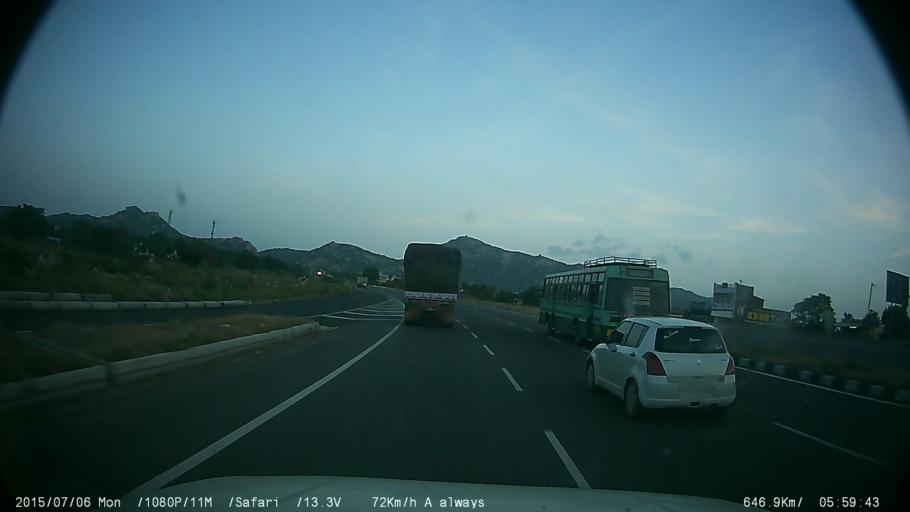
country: IN
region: Tamil Nadu
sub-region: Krishnagiri
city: Krishnagiri
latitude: 12.5970
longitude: 78.1366
